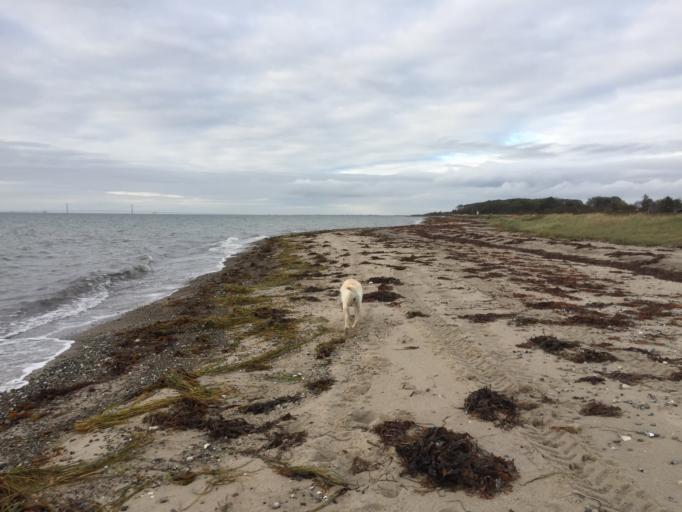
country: DK
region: Zealand
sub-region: Slagelse Kommune
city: Korsor
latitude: 55.2159
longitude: 11.1722
